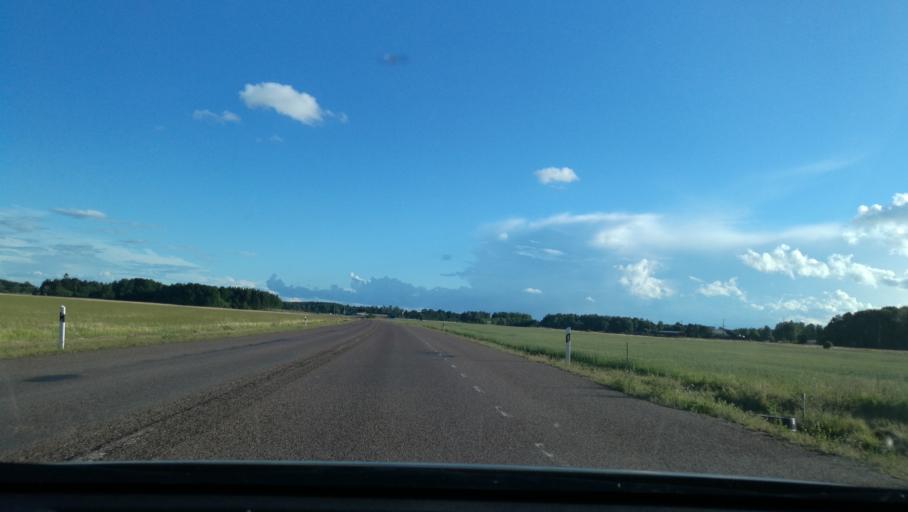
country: SE
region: Vaestmanland
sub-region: Kopings Kommun
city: Koping
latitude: 59.4898
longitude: 15.9876
